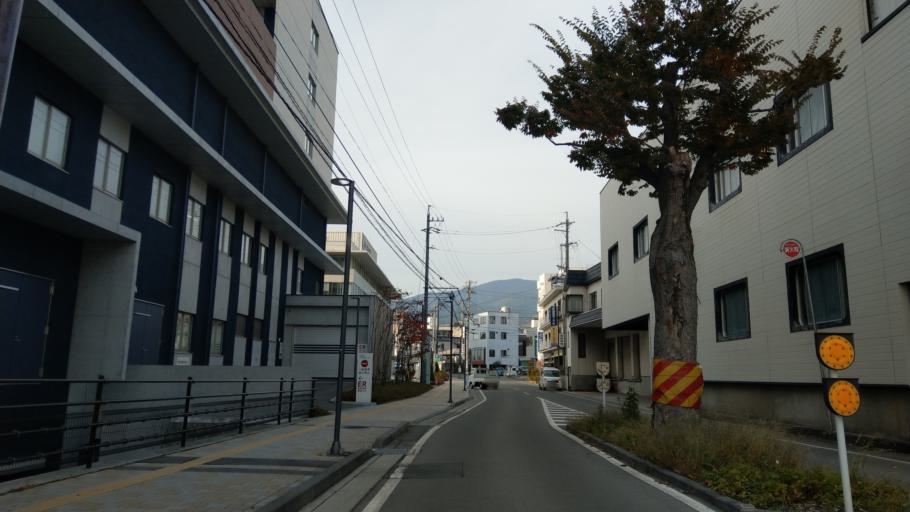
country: JP
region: Nagano
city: Komoro
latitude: 36.3264
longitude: 138.4264
